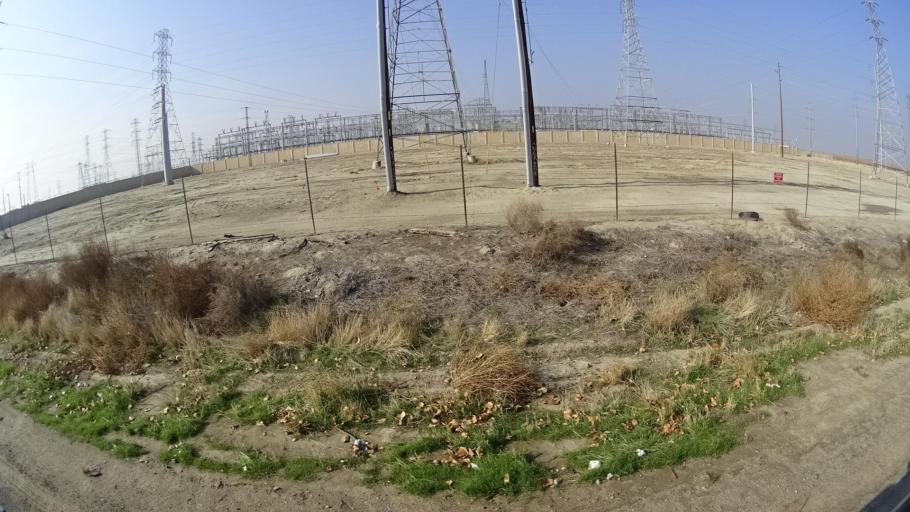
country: US
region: California
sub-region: Kern County
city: Buttonwillow
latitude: 35.4033
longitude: -119.4476
